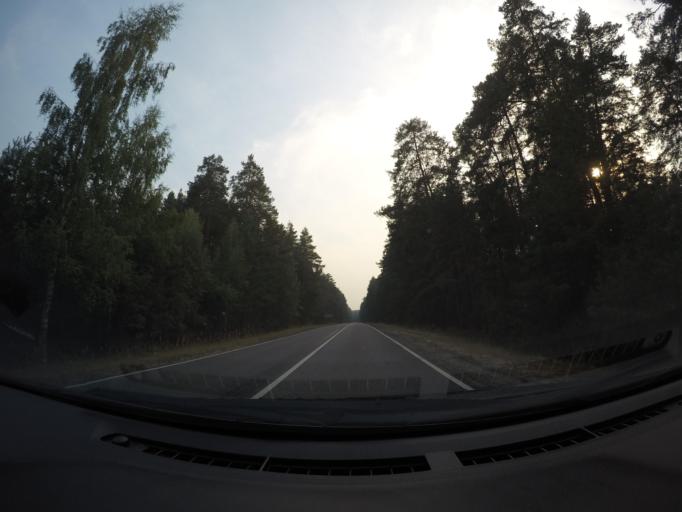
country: RU
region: Moskovskaya
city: Imeni Tsyurupy
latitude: 55.5138
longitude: 38.7222
